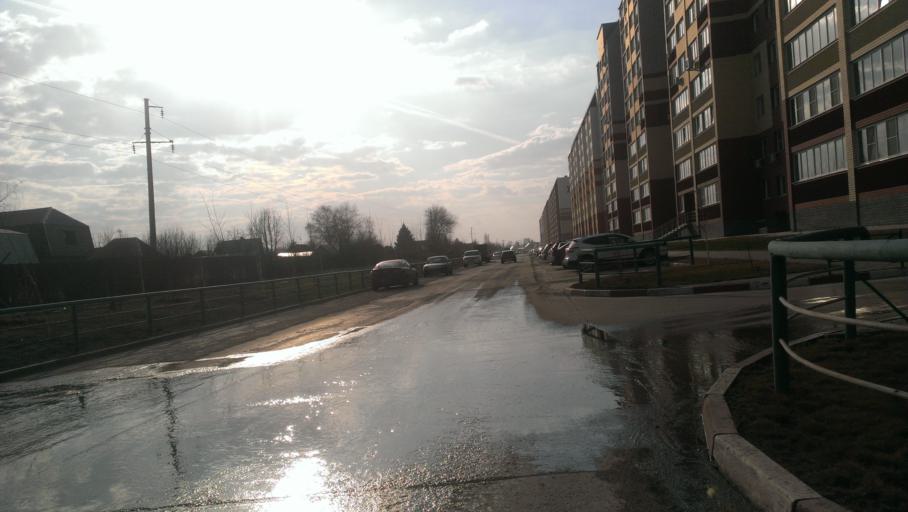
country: RU
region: Altai Krai
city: Novosilikatnyy
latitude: 53.3249
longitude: 83.6790
